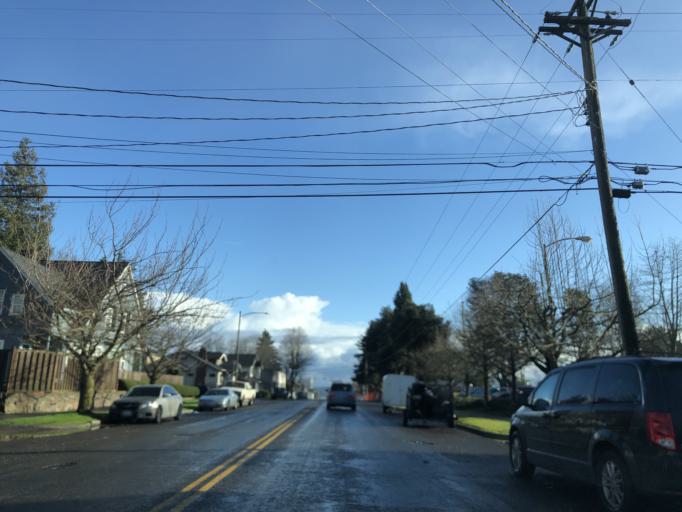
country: US
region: Washington
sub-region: Pierce County
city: Tacoma
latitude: 47.2538
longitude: -122.4546
